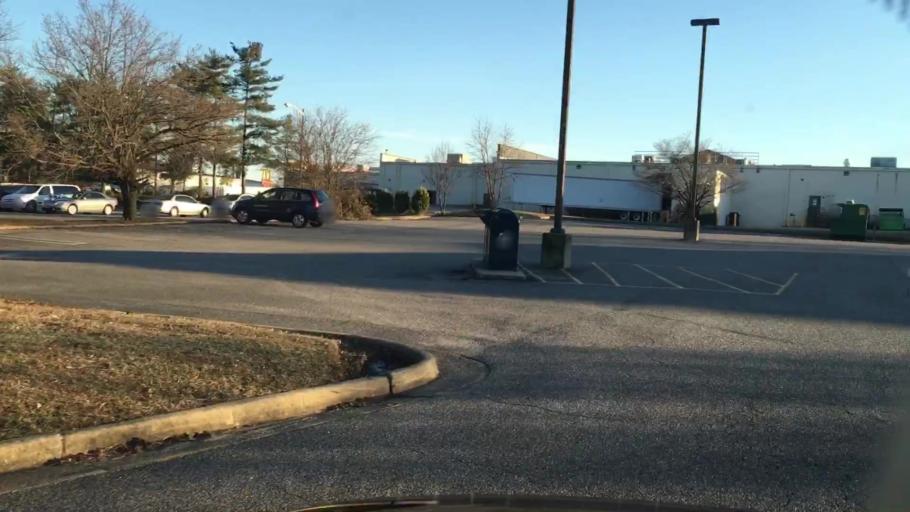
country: US
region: Virginia
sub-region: Chesterfield County
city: Bon Air
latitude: 37.5081
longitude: -77.6058
